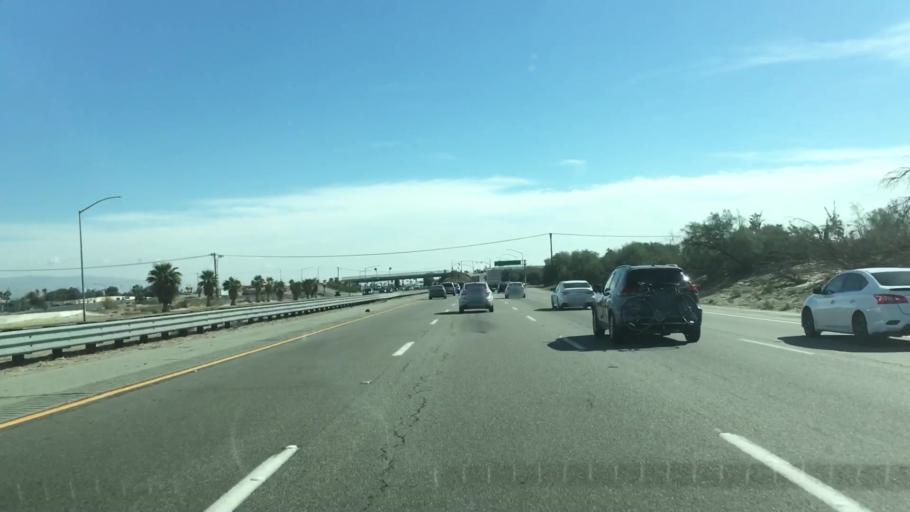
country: US
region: California
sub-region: Riverside County
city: Thousand Palms
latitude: 33.8093
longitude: -116.3941
